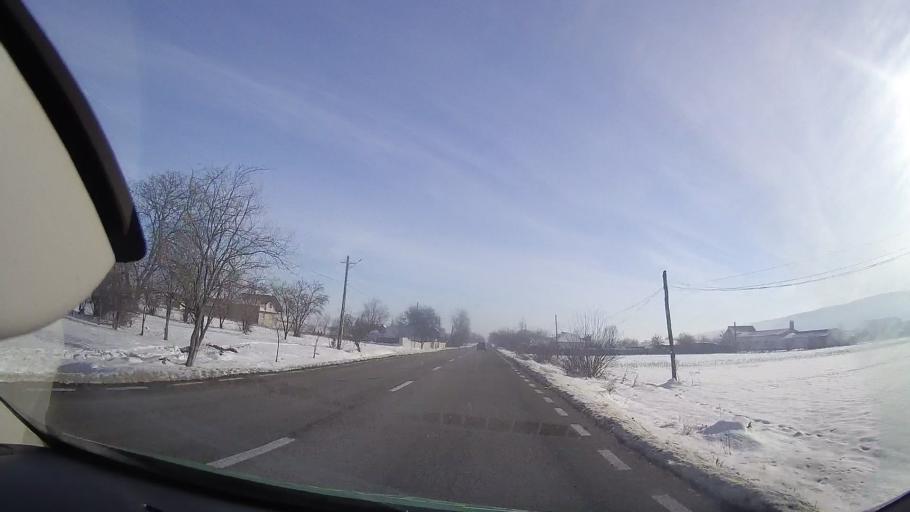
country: RO
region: Neamt
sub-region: Comuna Negresti
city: Negresti
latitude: 47.0629
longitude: 26.3801
